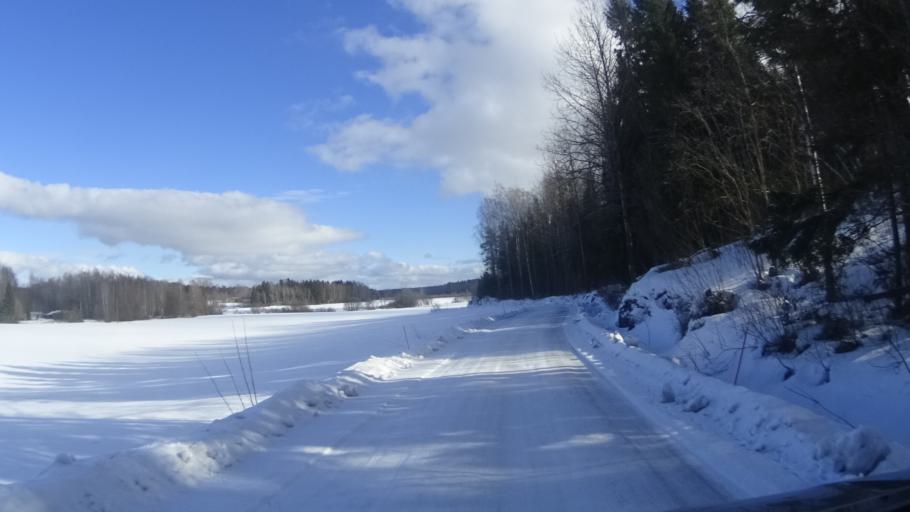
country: FI
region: Uusimaa
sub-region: Helsinki
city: Vantaa
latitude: 60.2485
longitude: 25.1661
